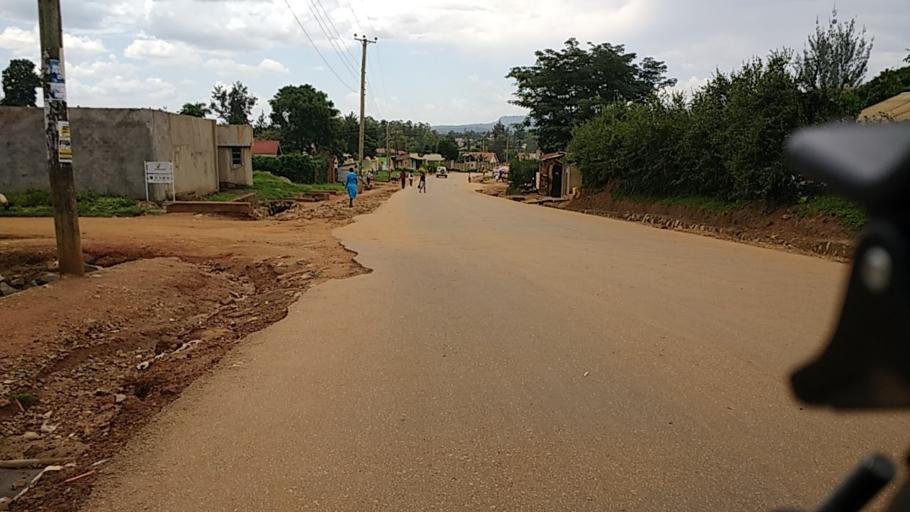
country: UG
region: Eastern Region
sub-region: Mbale District
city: Mbale
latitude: 1.0831
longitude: 34.1719
